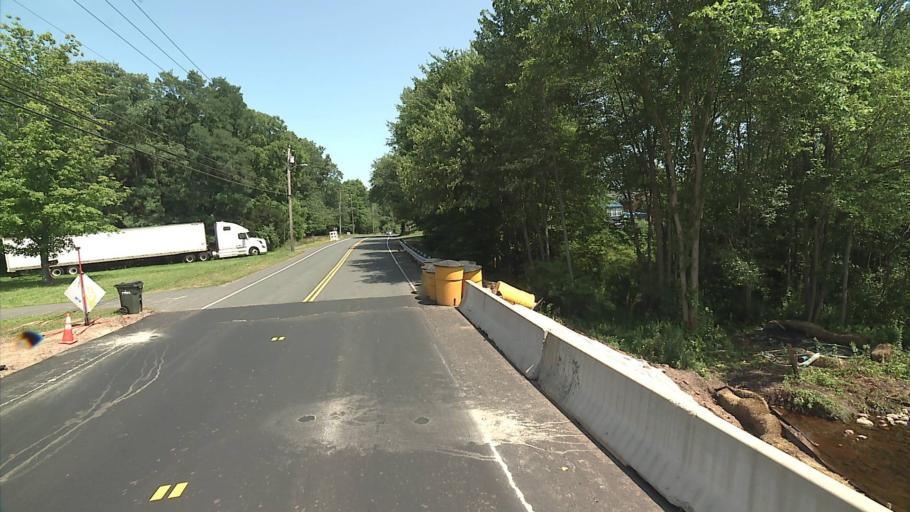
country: US
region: Connecticut
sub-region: Hartford County
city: Salmon Brook
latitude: 41.9527
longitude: -72.7630
